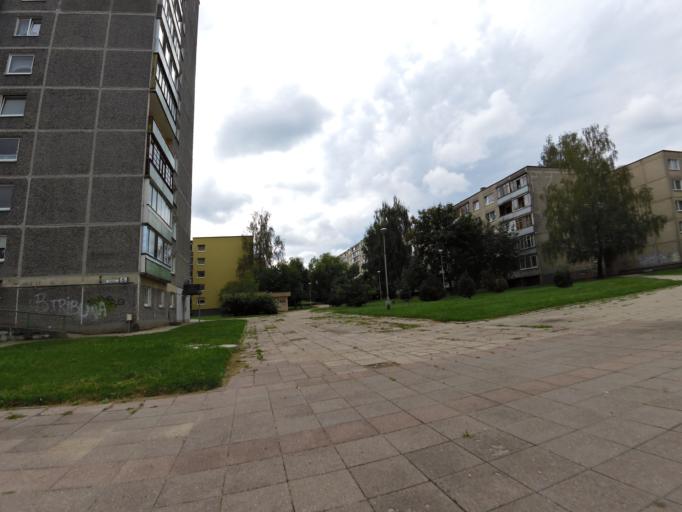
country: LT
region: Vilnius County
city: Lazdynai
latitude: 54.6760
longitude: 25.2081
